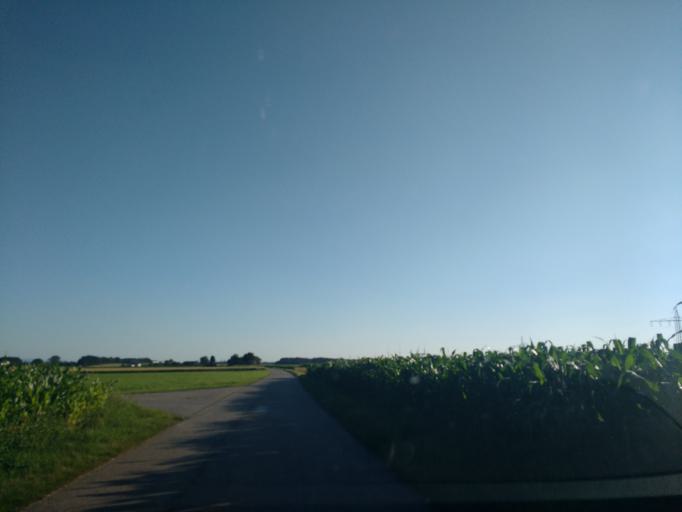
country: DE
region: Bavaria
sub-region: Upper Bavaria
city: Taufkirchen
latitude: 48.1468
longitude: 12.4742
